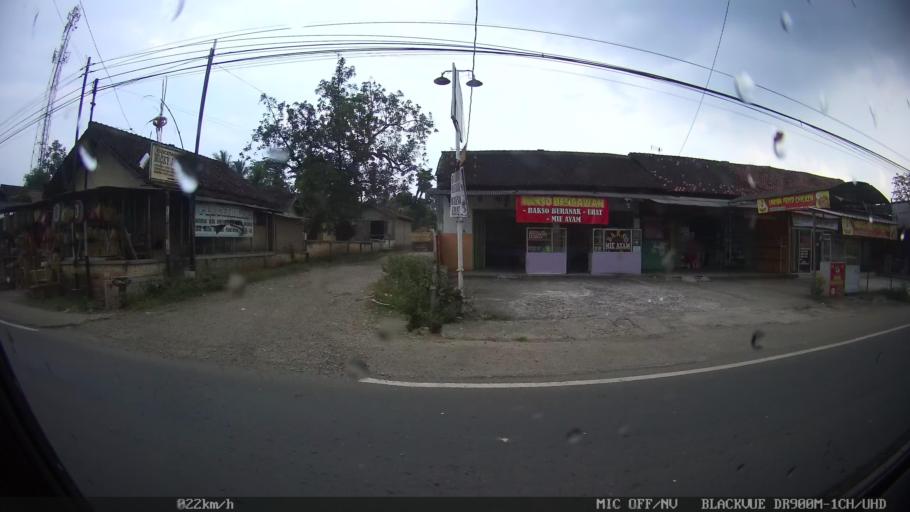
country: ID
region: Lampung
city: Gedongtataan
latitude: -5.3775
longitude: 105.1270
